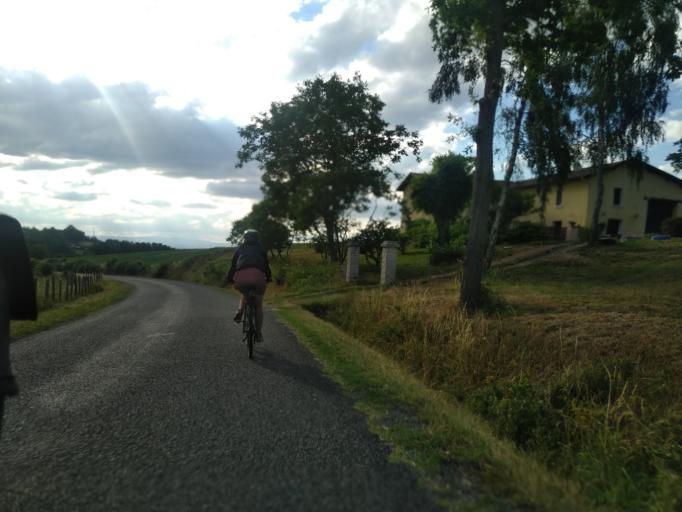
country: FR
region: Rhone-Alpes
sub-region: Departement du Rhone
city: Haute-Rivoire
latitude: 45.7259
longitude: 4.3531
